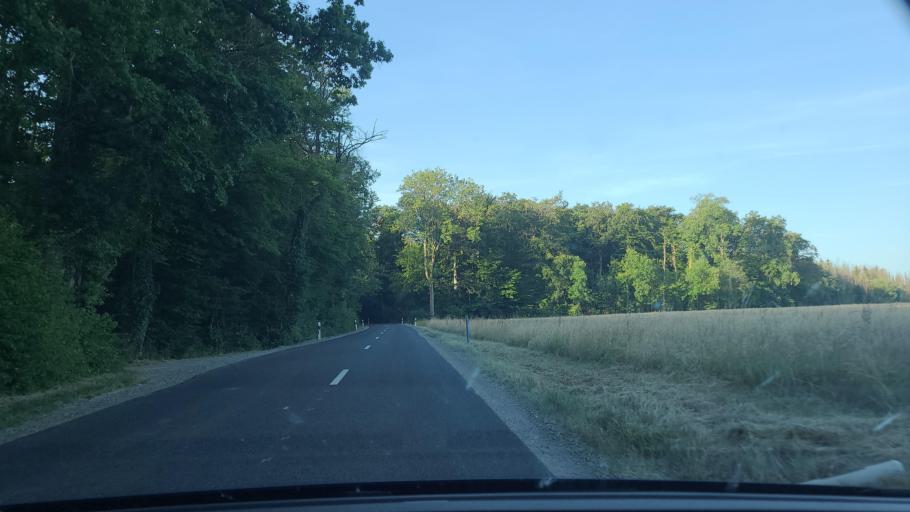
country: LU
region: Luxembourg
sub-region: Canton de Capellen
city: Dippach
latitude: 49.6033
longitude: 5.9909
